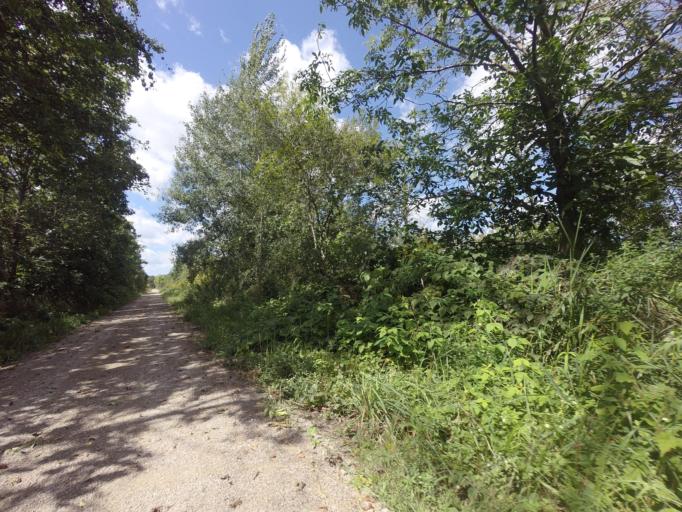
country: CA
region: Ontario
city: Huron East
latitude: 43.6317
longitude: -81.1818
